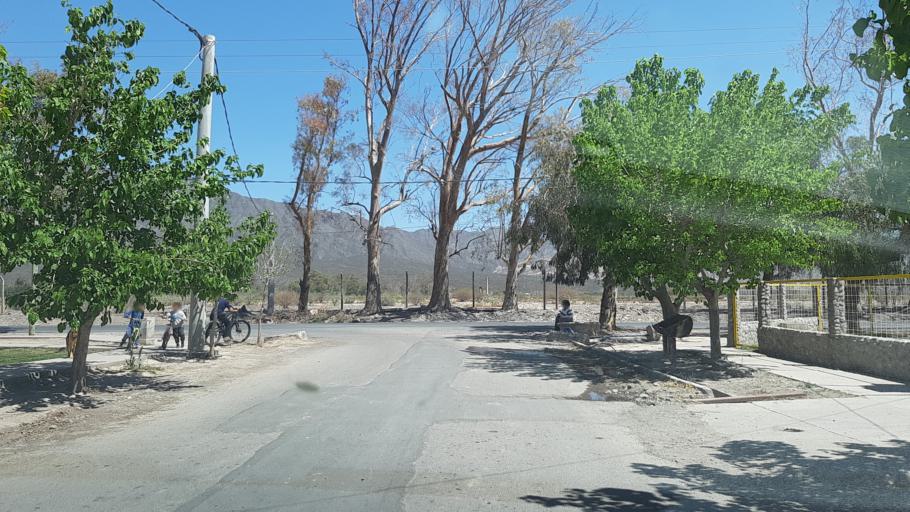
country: AR
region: San Juan
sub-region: Departamento de Zonda
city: Zonda
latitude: -31.5396
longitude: -68.7520
